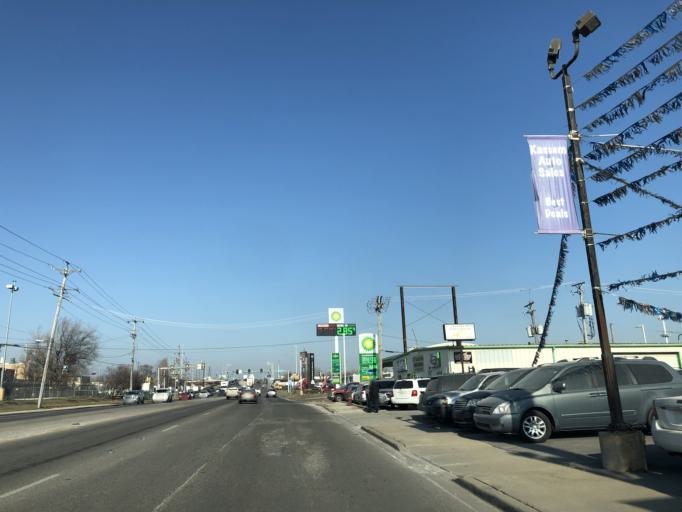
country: US
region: Illinois
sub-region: Cook County
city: Stickney
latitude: 41.8060
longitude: -87.7626
